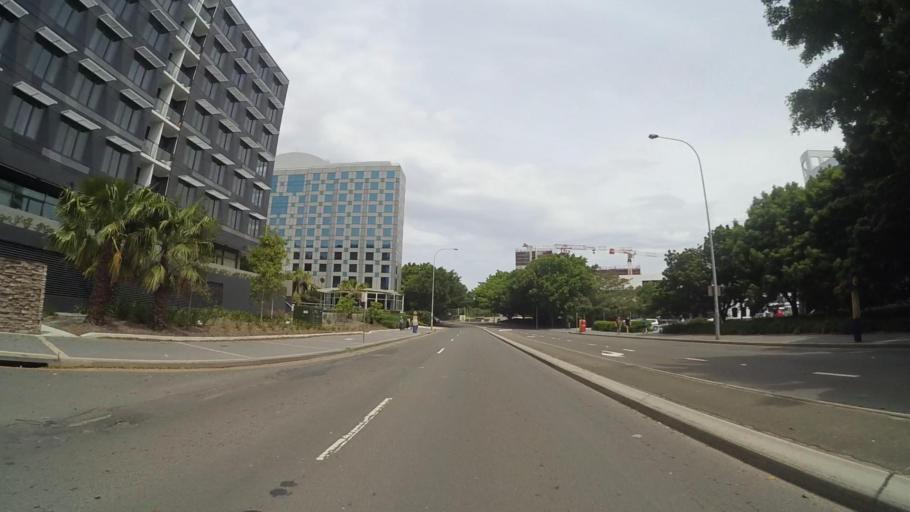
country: AU
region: New South Wales
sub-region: Botany Bay
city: Mascot
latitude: -33.9253
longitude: 151.1873
